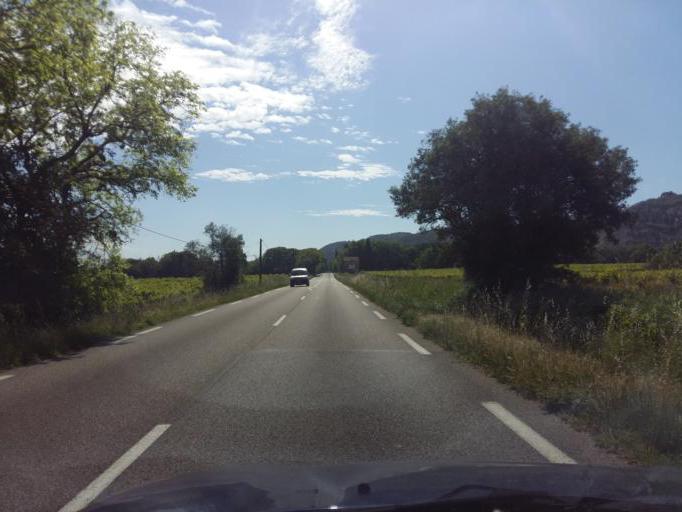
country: FR
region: Languedoc-Roussillon
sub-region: Departement du Gard
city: Montfaucon
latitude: 44.0583
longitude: 4.7431
